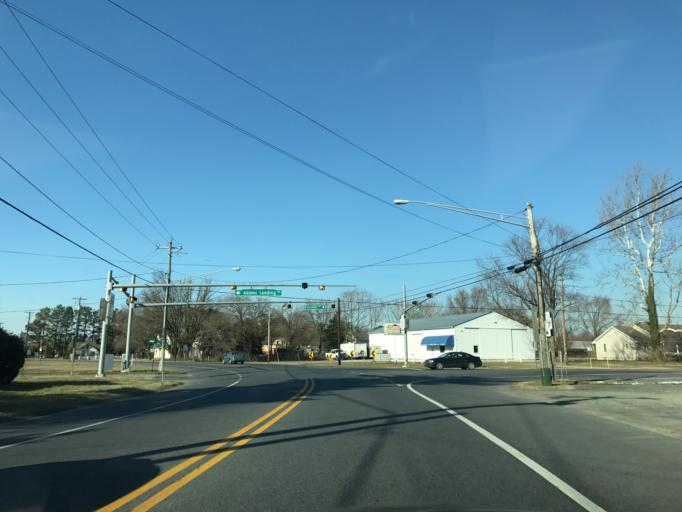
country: US
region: Maryland
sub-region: Caroline County
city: Denton
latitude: 38.9048
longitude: -75.8145
